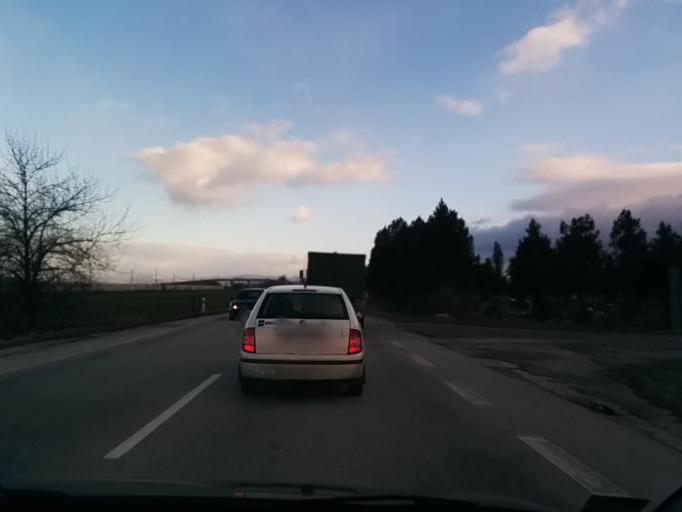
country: SK
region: Nitriansky
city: Cachtice
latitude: 48.6723
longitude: 17.8453
